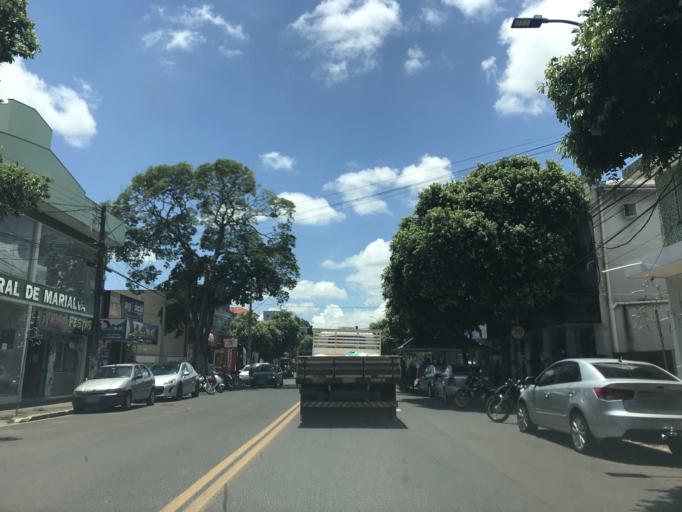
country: BR
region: Parana
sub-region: Marialva
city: Marialva
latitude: -23.4874
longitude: -51.7952
